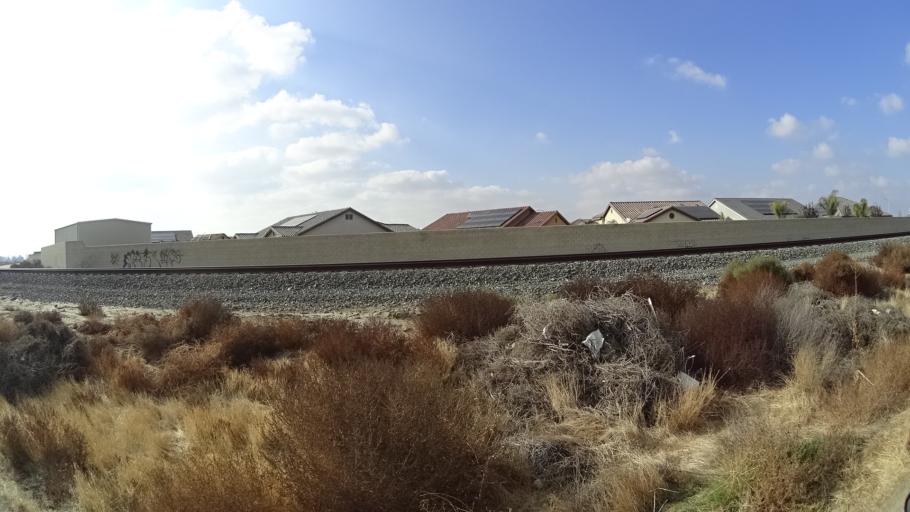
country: US
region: California
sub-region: Kern County
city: Greenacres
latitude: 35.2874
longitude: -119.1010
